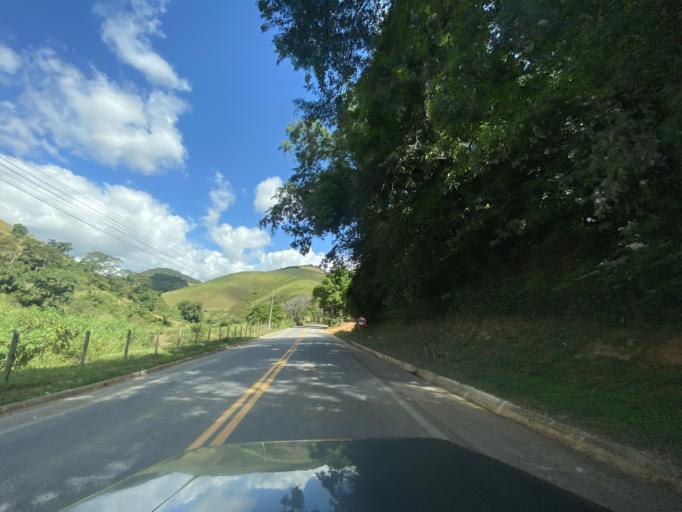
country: BR
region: Espirito Santo
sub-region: Alegre
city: Alegre
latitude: -20.7646
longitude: -41.5091
